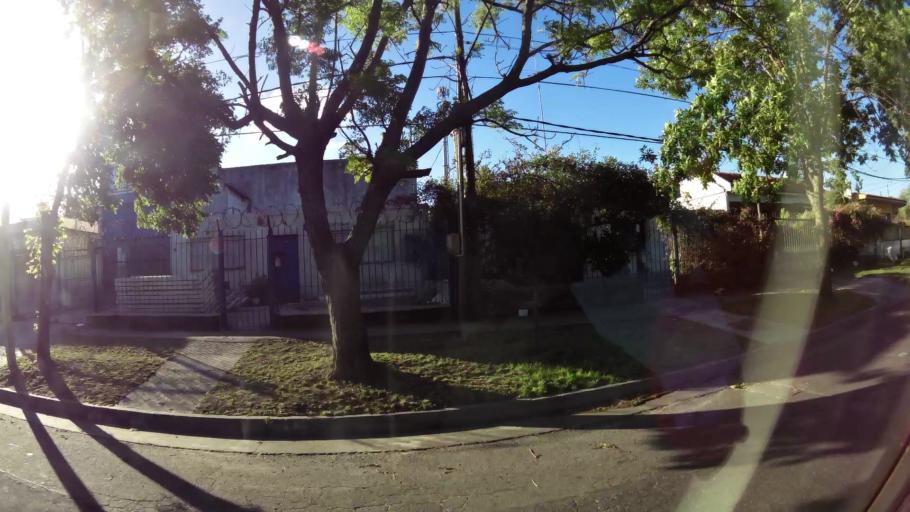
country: UY
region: Montevideo
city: Montevideo
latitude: -34.8822
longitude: -56.1300
